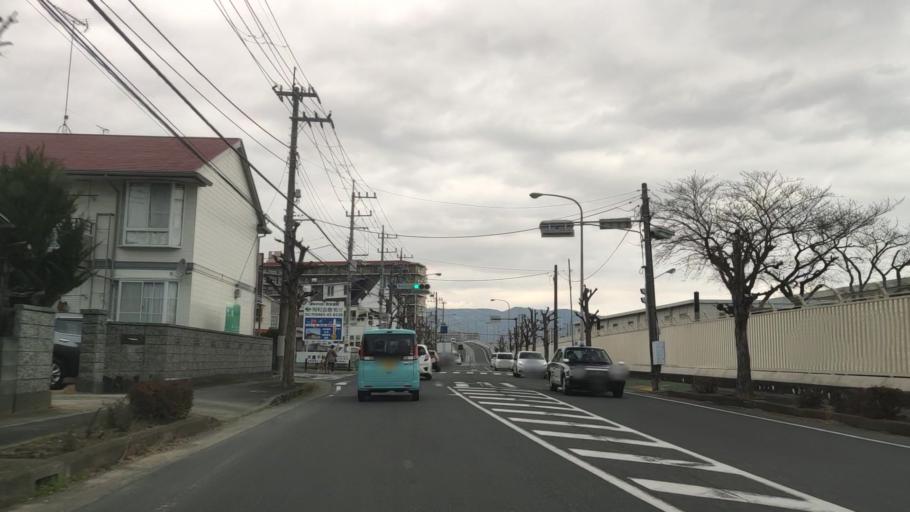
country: JP
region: Kanagawa
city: Odawara
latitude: 35.2739
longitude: 139.1890
